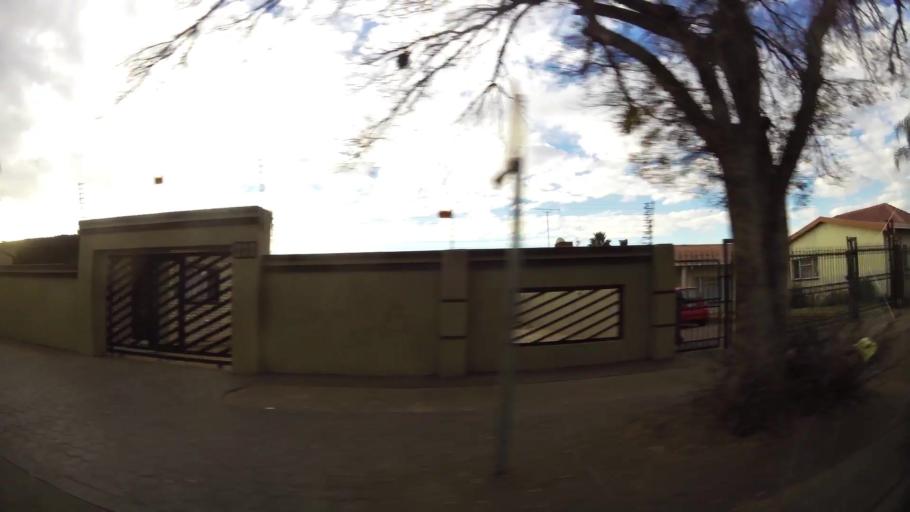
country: ZA
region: Gauteng
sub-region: City of Tshwane Metropolitan Municipality
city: Pretoria
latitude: -25.7150
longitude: 28.3090
